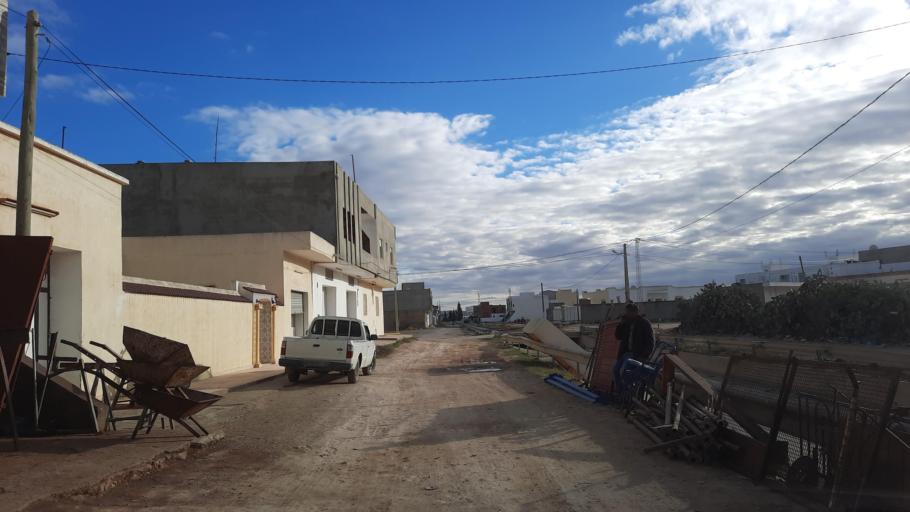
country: TN
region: Al Mahdiyah
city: El Jem
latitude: 35.2896
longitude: 10.7034
